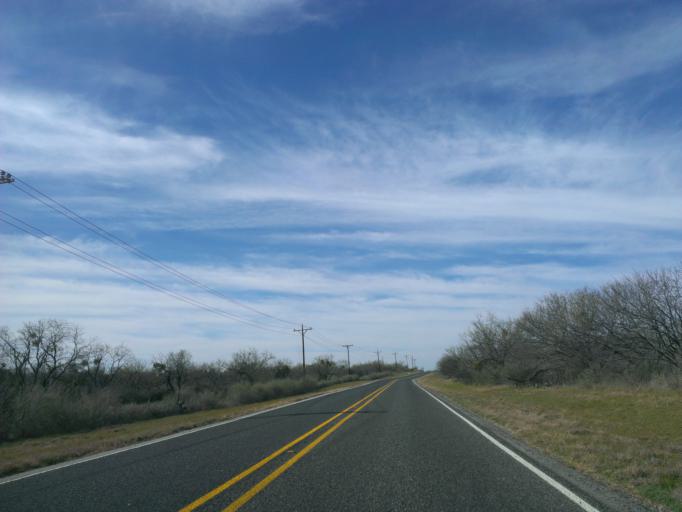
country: US
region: Texas
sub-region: Burnet County
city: Granite Shoals
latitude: 30.5940
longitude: -98.4362
